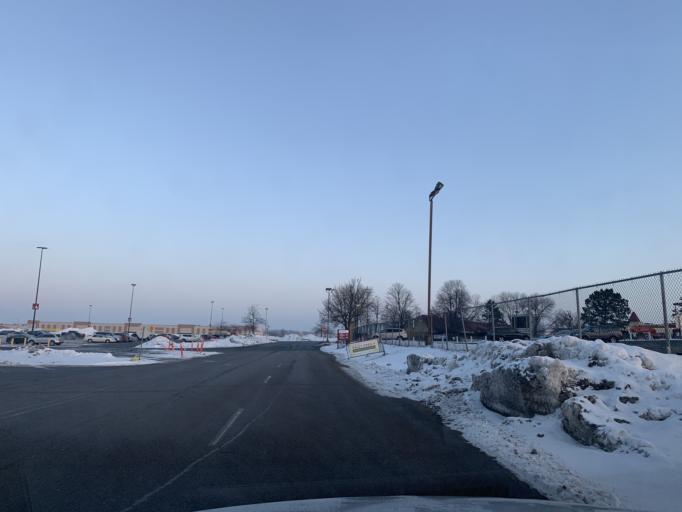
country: US
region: Minnesota
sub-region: Scott County
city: Shakopee
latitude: 44.7897
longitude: -93.4847
